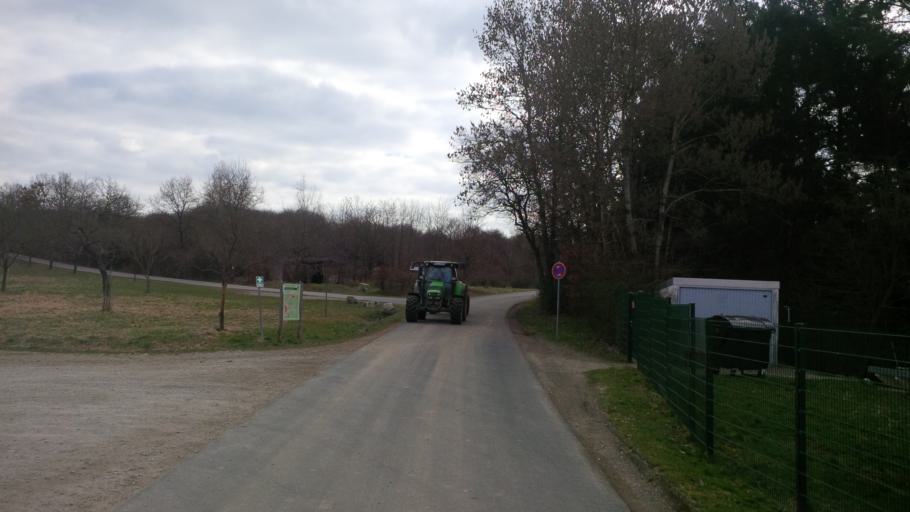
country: DE
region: Hesse
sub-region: Regierungsbezirk Darmstadt
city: Wehrheim
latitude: 50.3038
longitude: 8.5876
